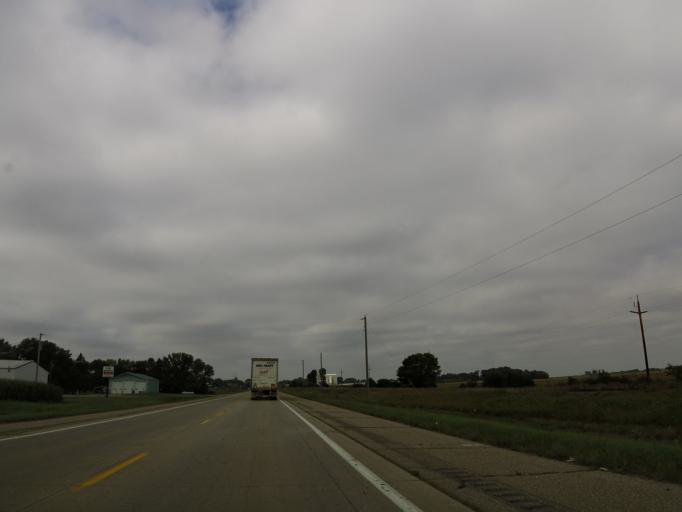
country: US
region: Minnesota
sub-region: Renville County
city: Olivia
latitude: 44.7752
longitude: -94.9650
